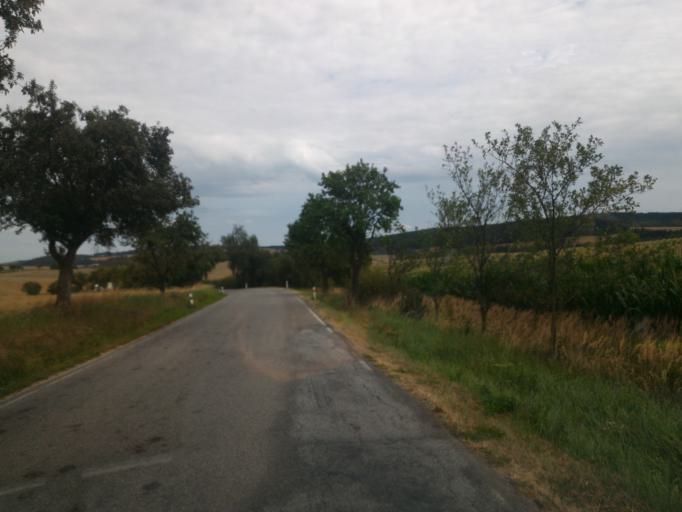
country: CZ
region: Vysocina
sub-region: Okres Jihlava
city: Telc
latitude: 49.1218
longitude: 15.5209
